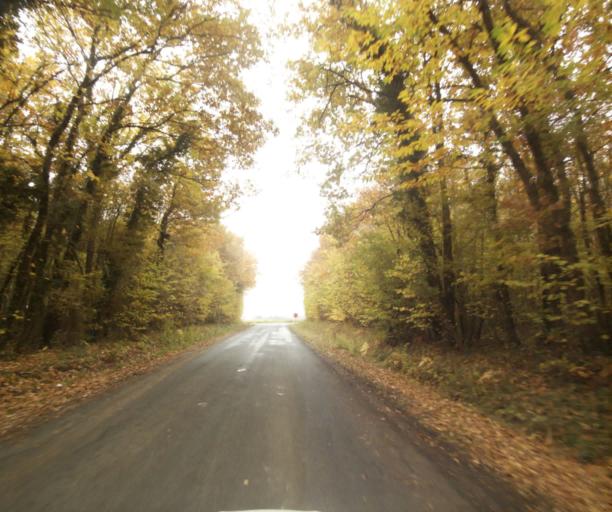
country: FR
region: Poitou-Charentes
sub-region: Departement de la Charente-Maritime
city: Chermignac
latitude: 45.7092
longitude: -0.6914
